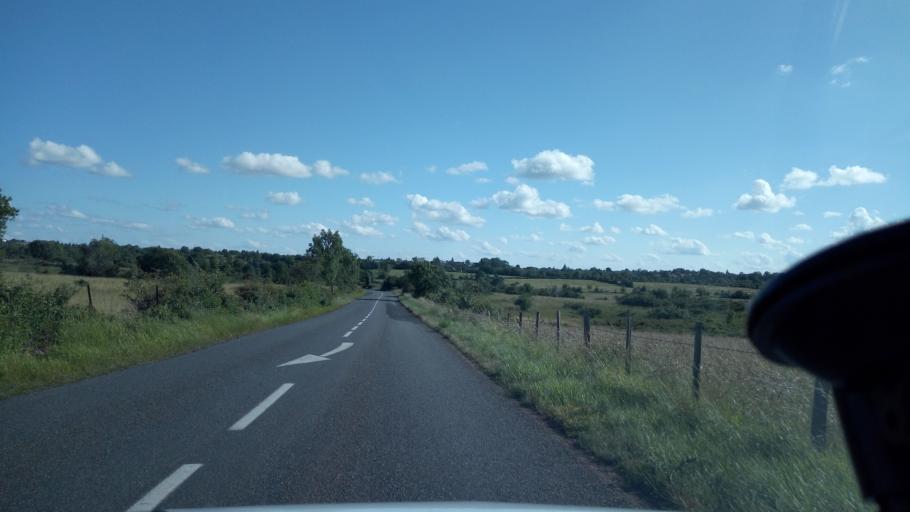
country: FR
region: Midi-Pyrenees
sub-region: Departement de l'Aveyron
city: Sebazac-Concoures
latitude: 44.4199
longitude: 2.6085
